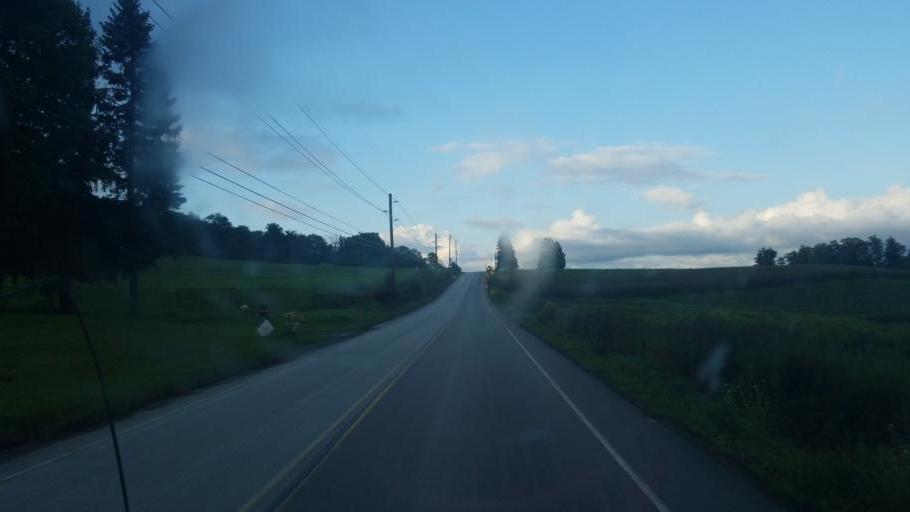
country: US
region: Pennsylvania
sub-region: Potter County
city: Galeton
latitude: 41.8545
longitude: -77.7685
